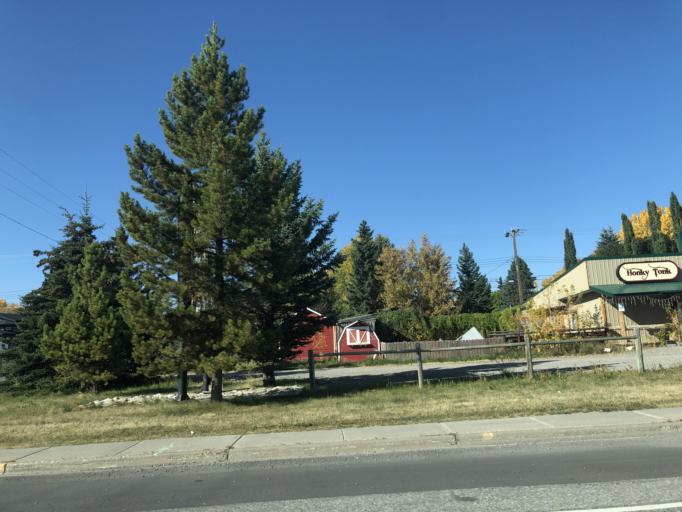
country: CA
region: Alberta
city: Black Diamond
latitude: 50.5327
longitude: -114.2309
